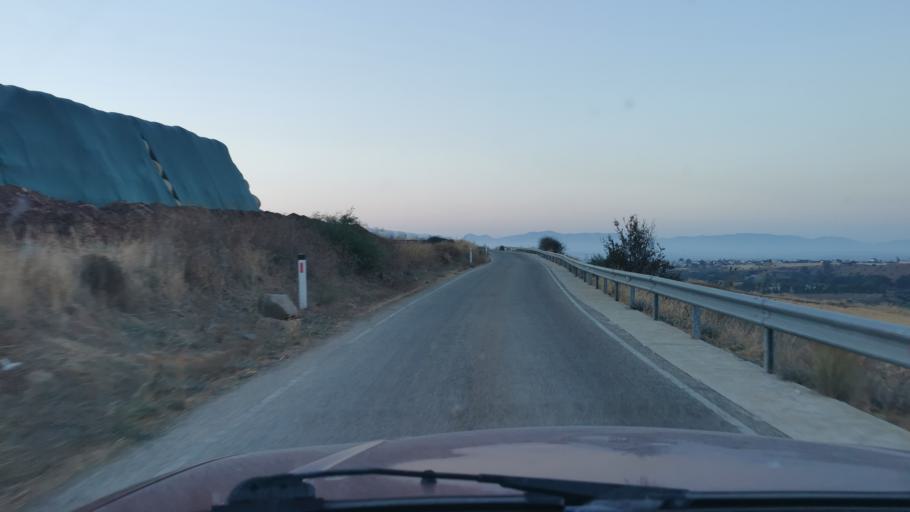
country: CY
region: Lefkosia
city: Peristerona
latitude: 35.0800
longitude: 33.0818
